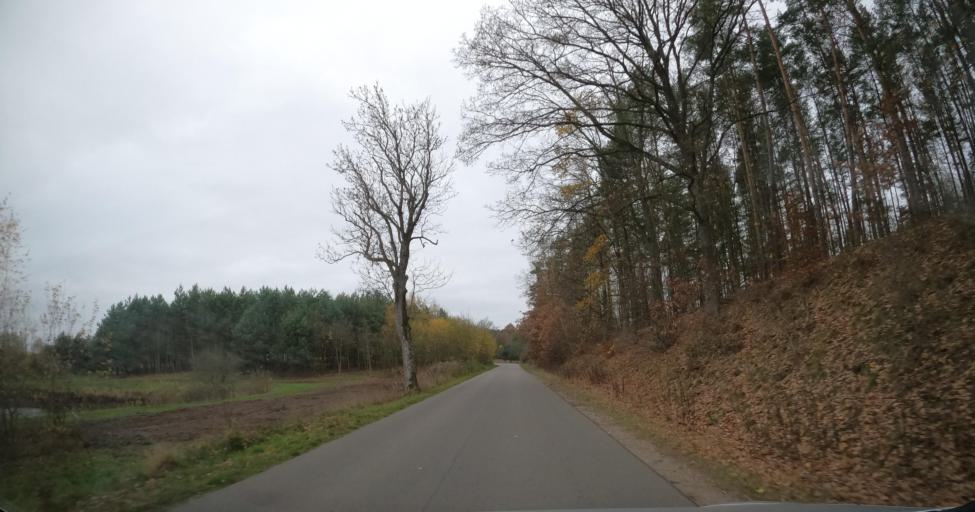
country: PL
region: West Pomeranian Voivodeship
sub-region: Powiat swidwinski
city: Polczyn-Zdroj
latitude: 53.7820
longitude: 16.1729
